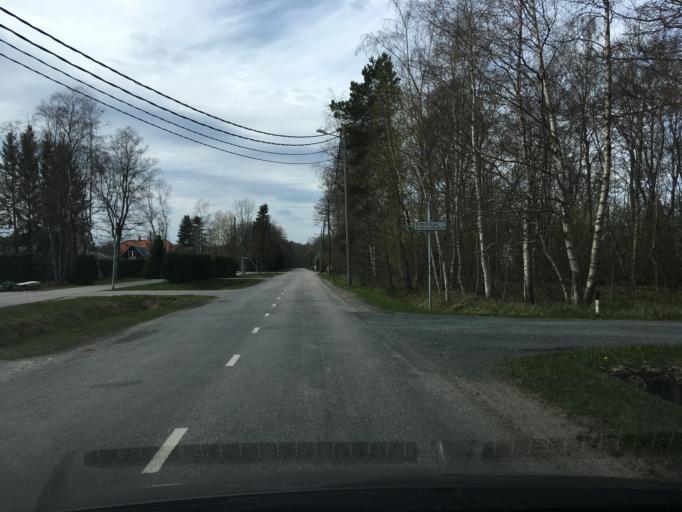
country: EE
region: Harju
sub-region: Joelaehtme vald
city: Loo
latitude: 59.4754
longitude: 24.9264
